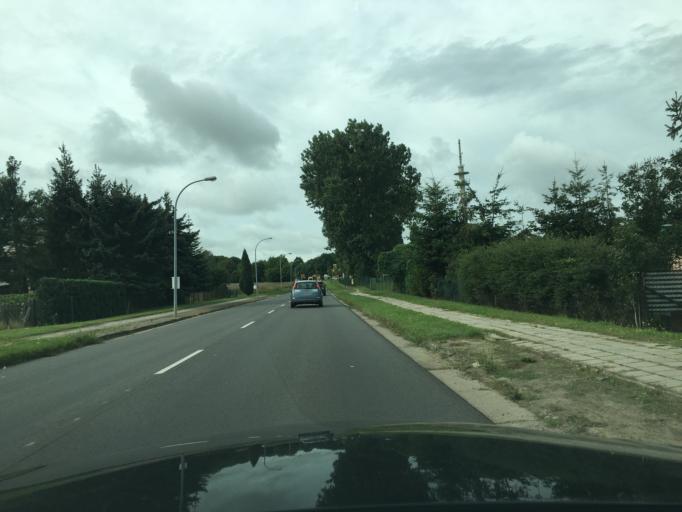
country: DE
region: Brandenburg
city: Gransee
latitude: 53.0011
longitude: 13.1578
